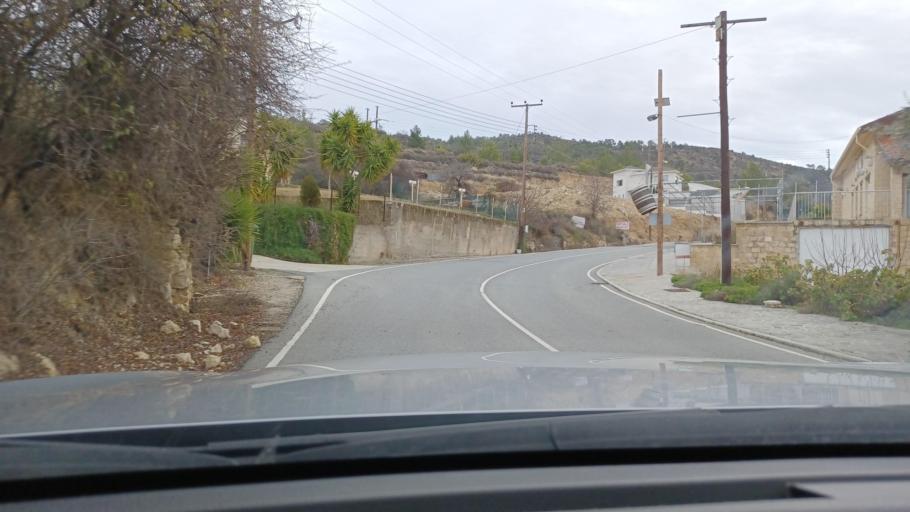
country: CY
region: Limassol
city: Pelendri
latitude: 34.8071
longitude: 32.9148
